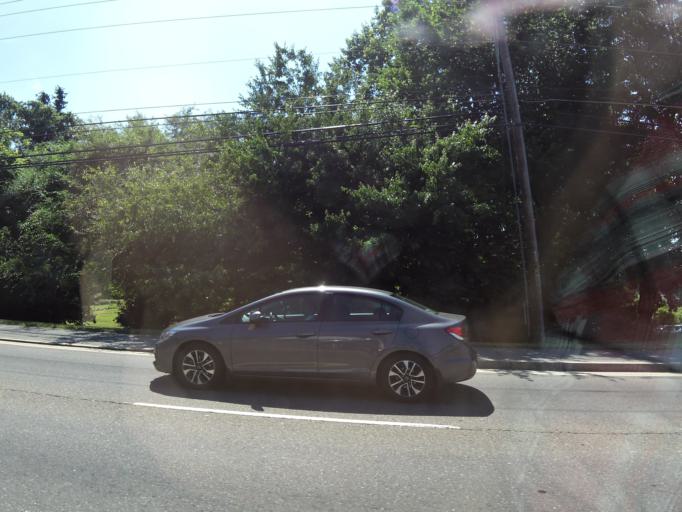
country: US
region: Tennessee
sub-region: Sevier County
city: Pigeon Forge
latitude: 35.8198
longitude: -83.5784
